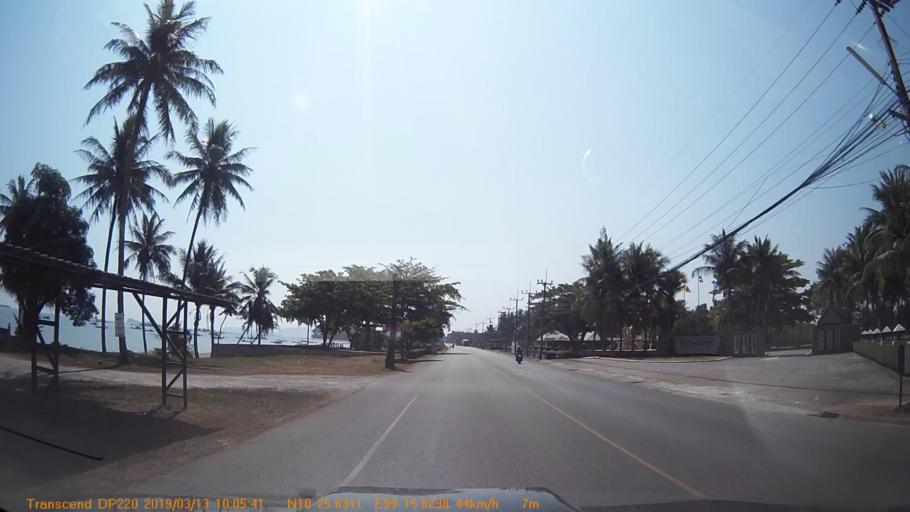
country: TH
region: Chumphon
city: Chumphon
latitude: 10.4270
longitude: 99.2640
